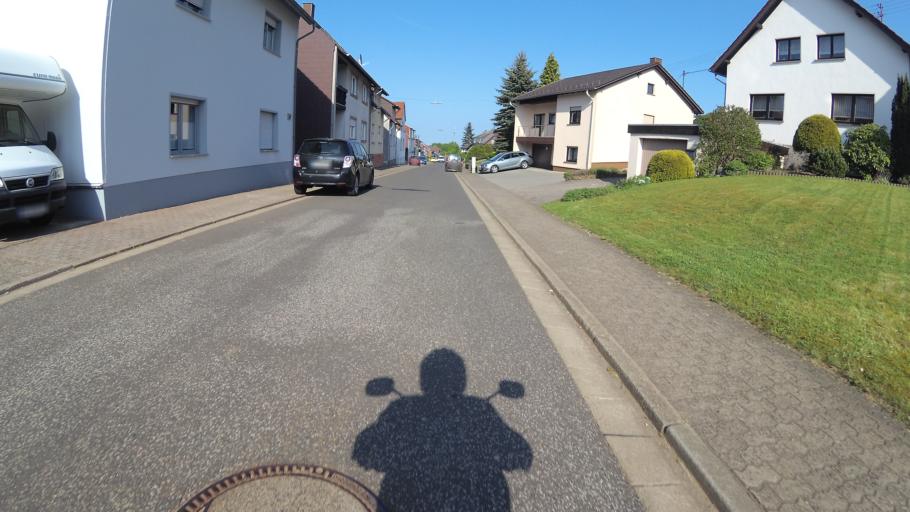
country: DE
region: Saarland
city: Eppelborn
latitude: 49.3938
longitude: 7.0062
